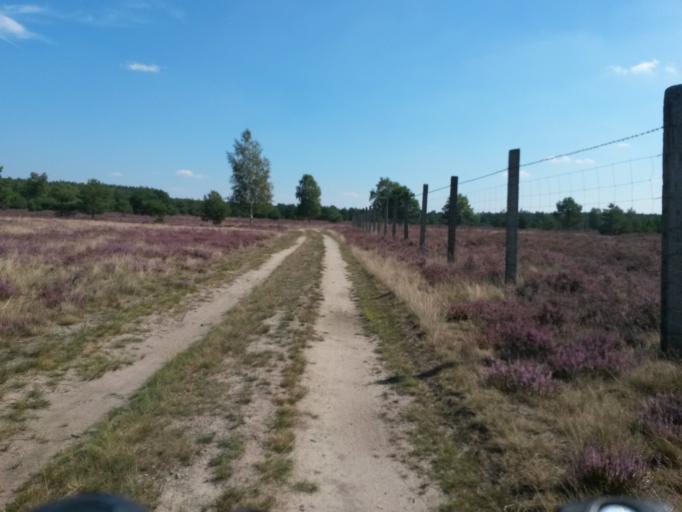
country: DE
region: Brandenburg
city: Milmersdorf
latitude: 53.0332
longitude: 13.5705
